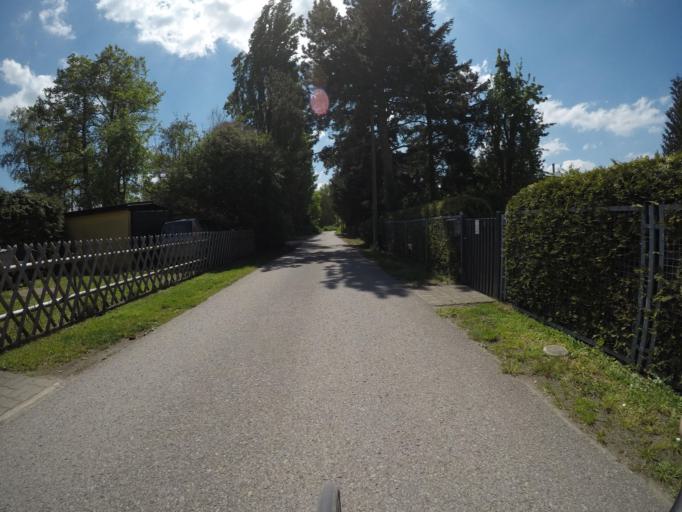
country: DE
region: Brandenburg
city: Werder
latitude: 52.4035
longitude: 12.9462
